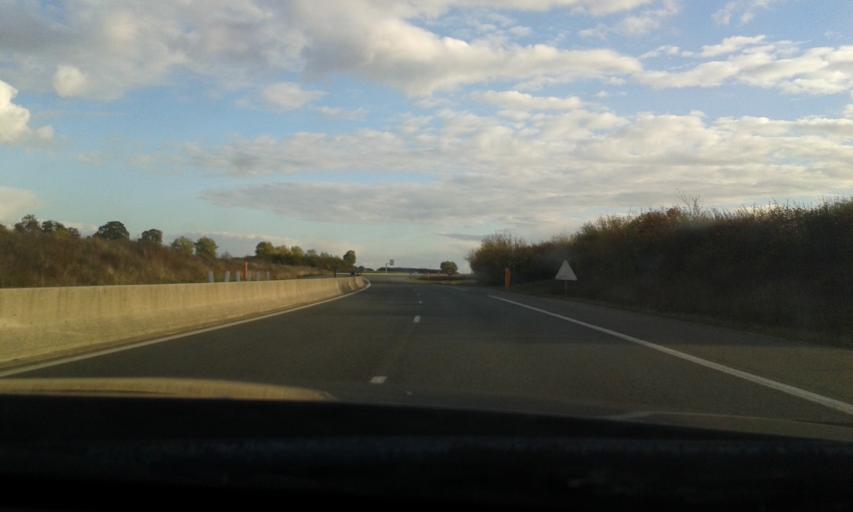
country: FR
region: Centre
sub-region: Departement d'Eure-et-Loir
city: Luray
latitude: 48.6730
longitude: 1.3846
